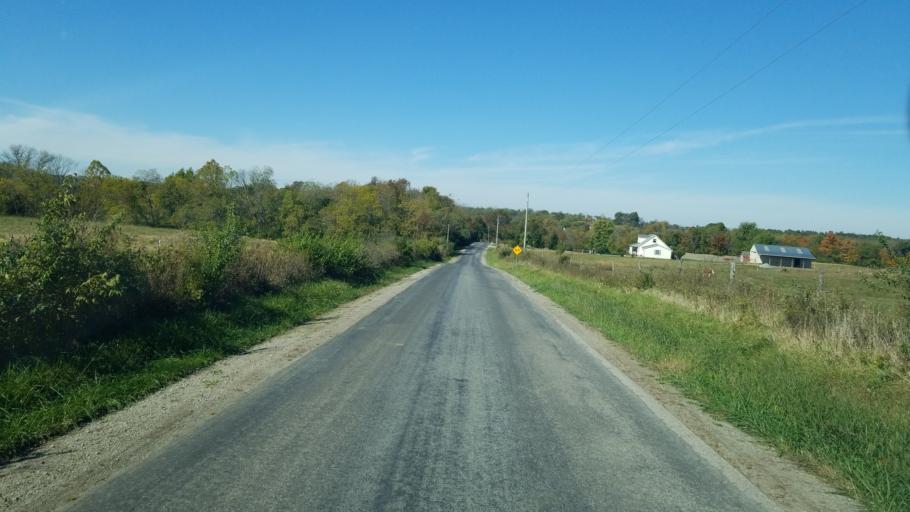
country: US
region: Ohio
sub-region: Highland County
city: Leesburg
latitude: 39.2756
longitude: -83.4661
